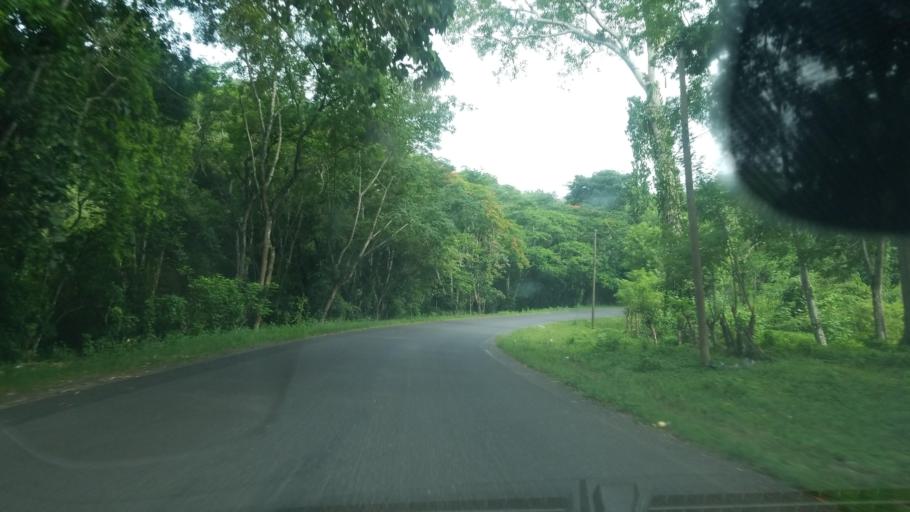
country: HN
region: Santa Barbara
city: Petoa
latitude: 15.2399
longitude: -88.2673
